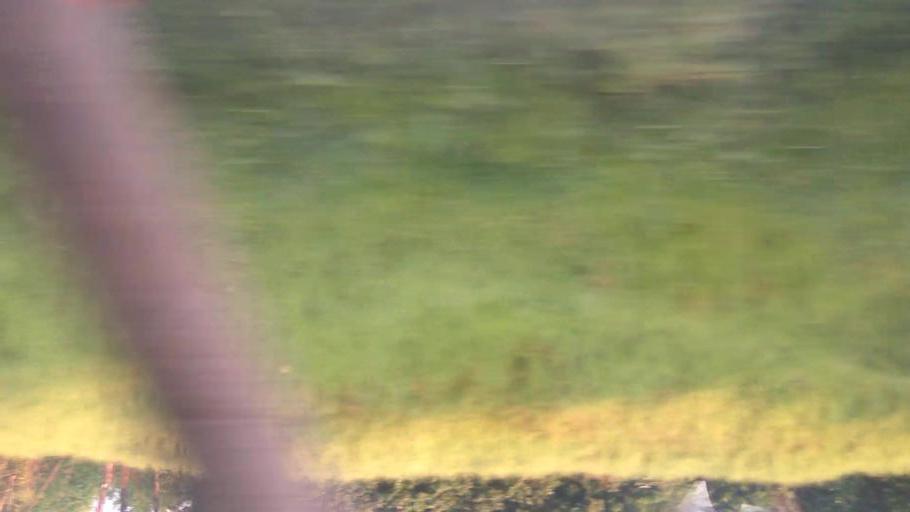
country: RU
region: Moskovskaya
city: Stupino
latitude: 54.8916
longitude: 38.0949
